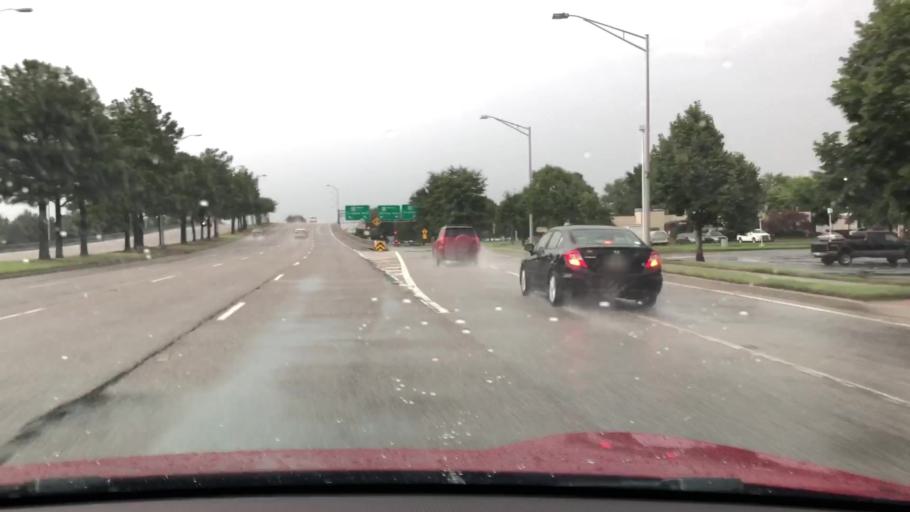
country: US
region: Virginia
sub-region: City of Chesapeake
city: Chesapeake
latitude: 36.8531
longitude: -76.2098
